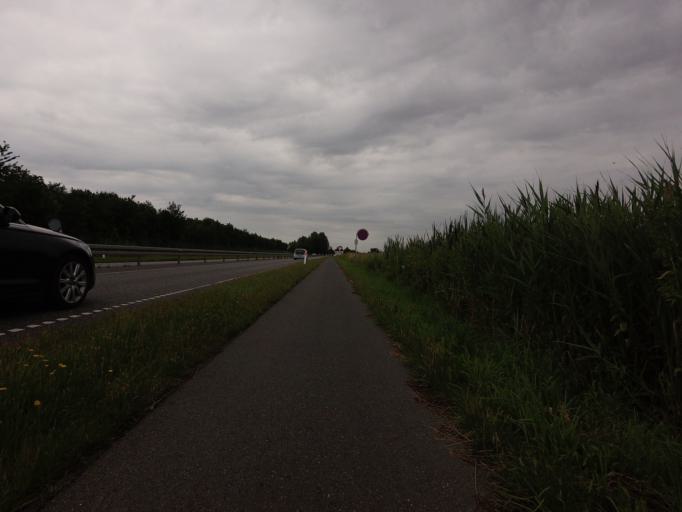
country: DK
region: North Denmark
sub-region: Alborg Kommune
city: Vadum
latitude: 57.0990
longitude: 9.8853
